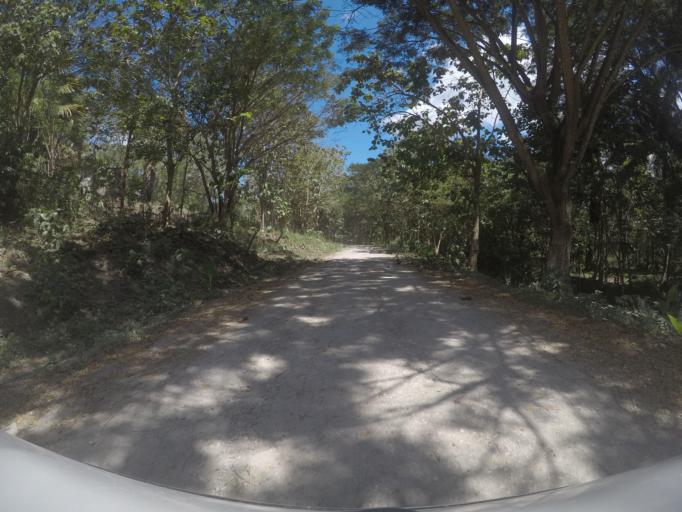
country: TL
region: Viqueque
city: Viqueque
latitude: -8.9068
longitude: 126.3927
